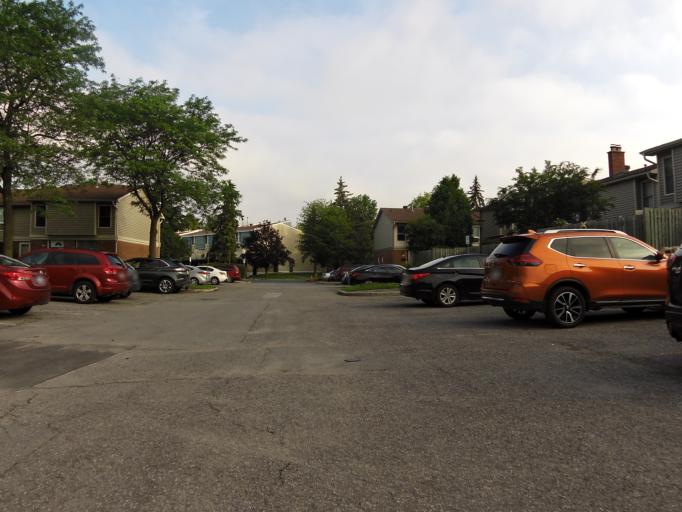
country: CA
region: Ontario
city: Ottawa
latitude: 45.3460
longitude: -75.6656
